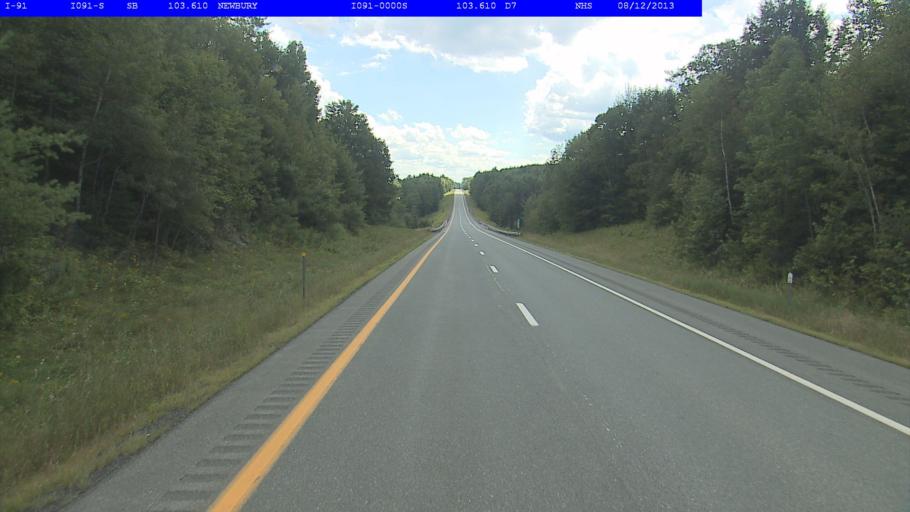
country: US
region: New Hampshire
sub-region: Grafton County
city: Haverhill
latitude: 44.0658
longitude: -72.1104
